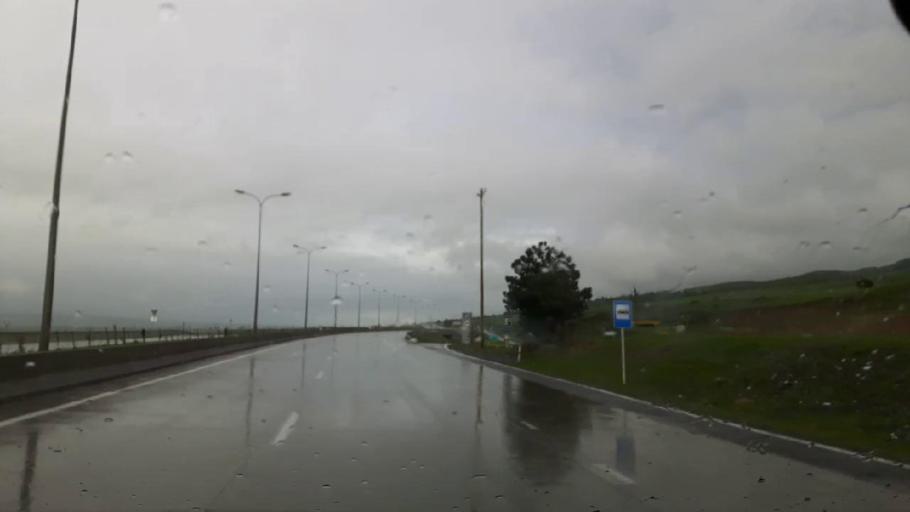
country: GE
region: Shida Kartli
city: Gori
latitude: 42.0260
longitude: 44.2044
